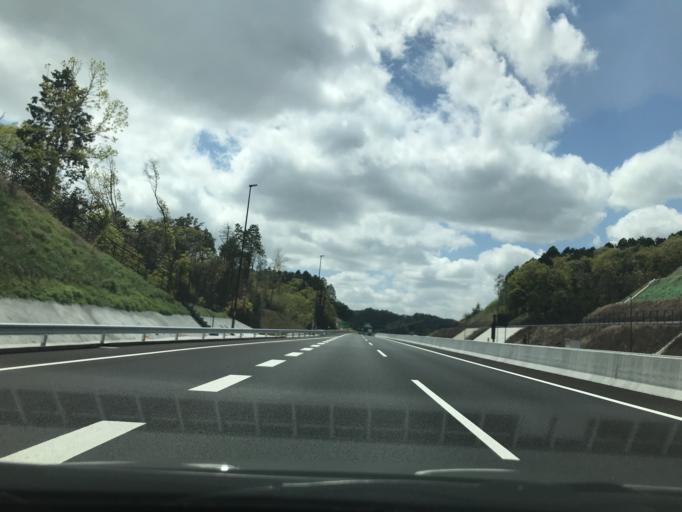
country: JP
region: Osaka
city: Ibaraki
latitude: 34.8787
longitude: 135.5281
